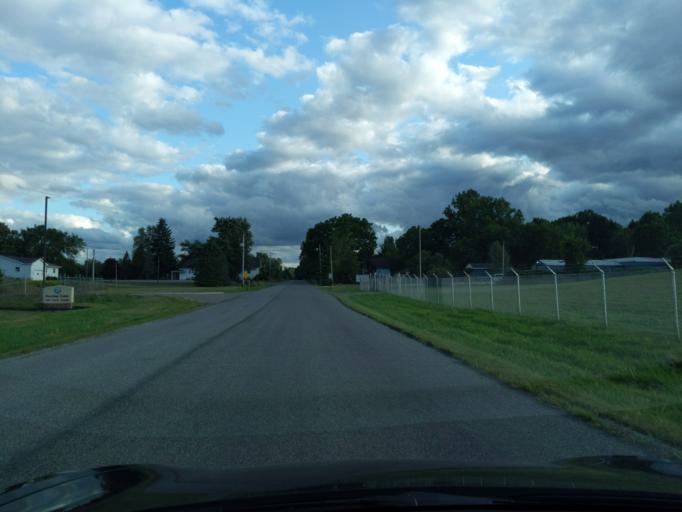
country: US
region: Michigan
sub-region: Ingham County
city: Holt
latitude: 42.6238
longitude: -84.5824
